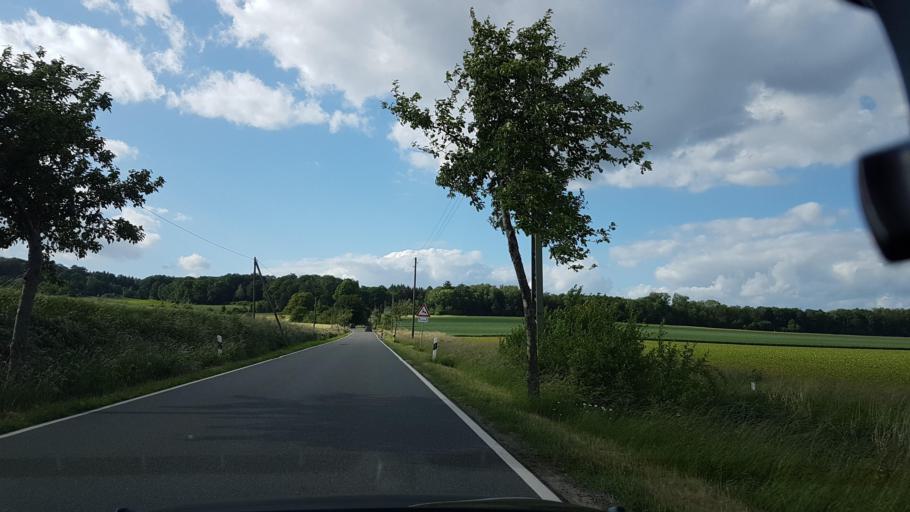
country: DE
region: Lower Saxony
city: Elze
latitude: 52.1187
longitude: 9.6808
